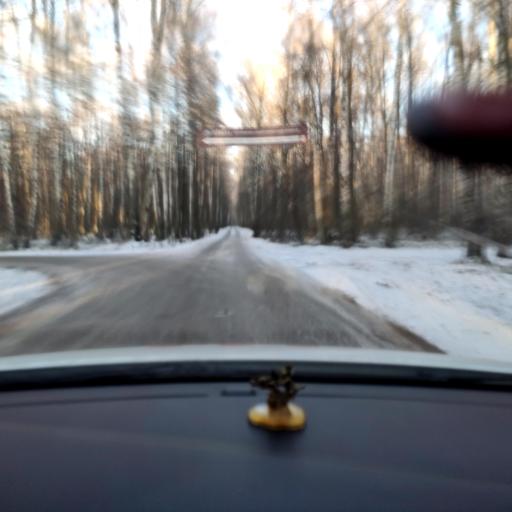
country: RU
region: Tatarstan
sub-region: Gorod Kazan'
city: Kazan
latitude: 55.6769
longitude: 49.0999
